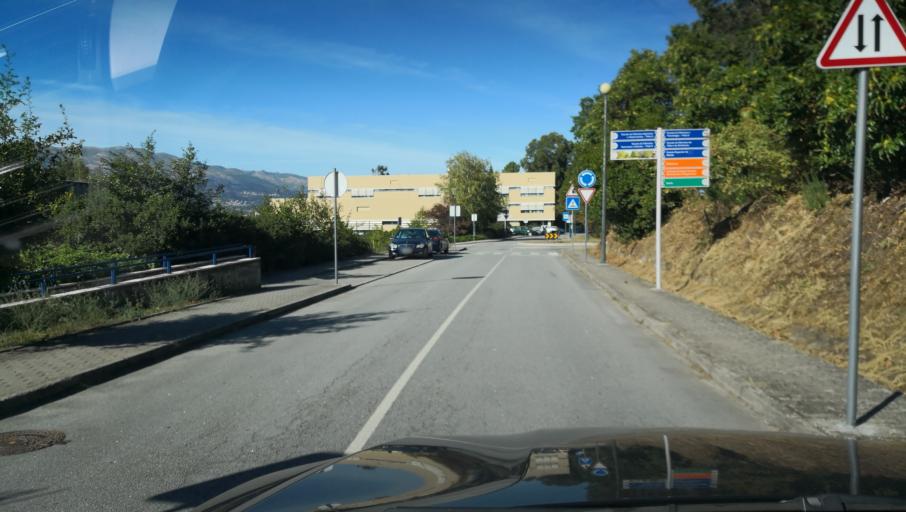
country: PT
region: Vila Real
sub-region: Vila Real
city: Vila Real
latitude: 41.2844
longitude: -7.7440
